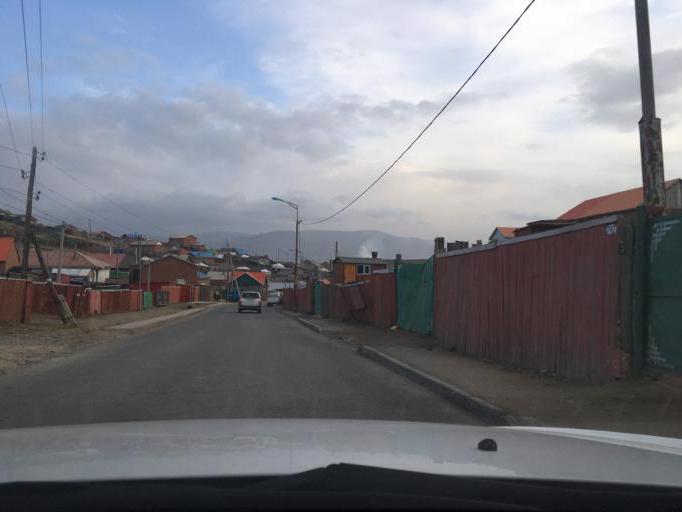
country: MN
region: Ulaanbaatar
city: Ulaanbaatar
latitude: 47.9301
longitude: 106.8583
